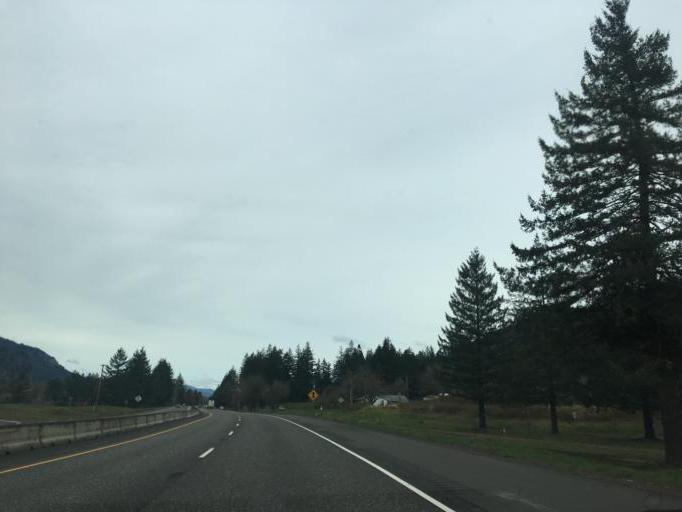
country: US
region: Oregon
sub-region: Hood River County
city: Cascade Locks
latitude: 45.6020
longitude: -122.0432
